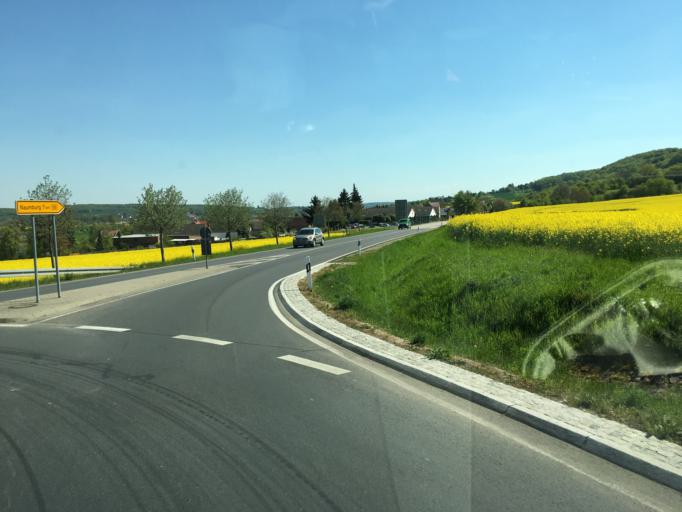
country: DE
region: Saxony-Anhalt
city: Freyburg
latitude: 51.2027
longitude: 11.7694
